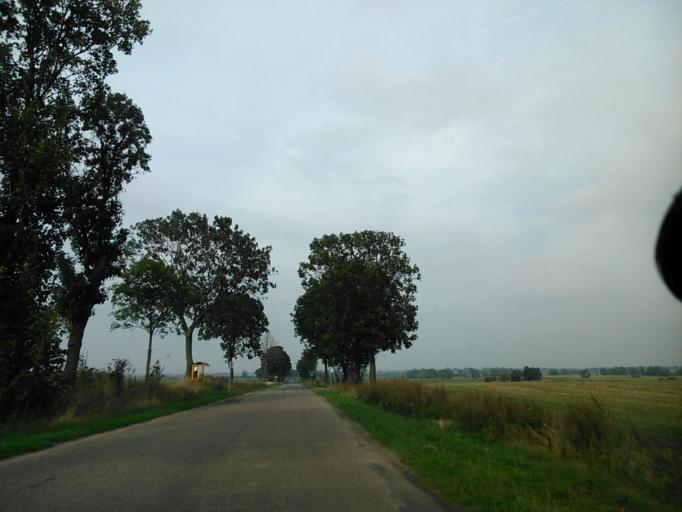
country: PL
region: Kujawsko-Pomorskie
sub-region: Powiat wabrzeski
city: Pluznica
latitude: 53.2373
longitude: 18.8166
